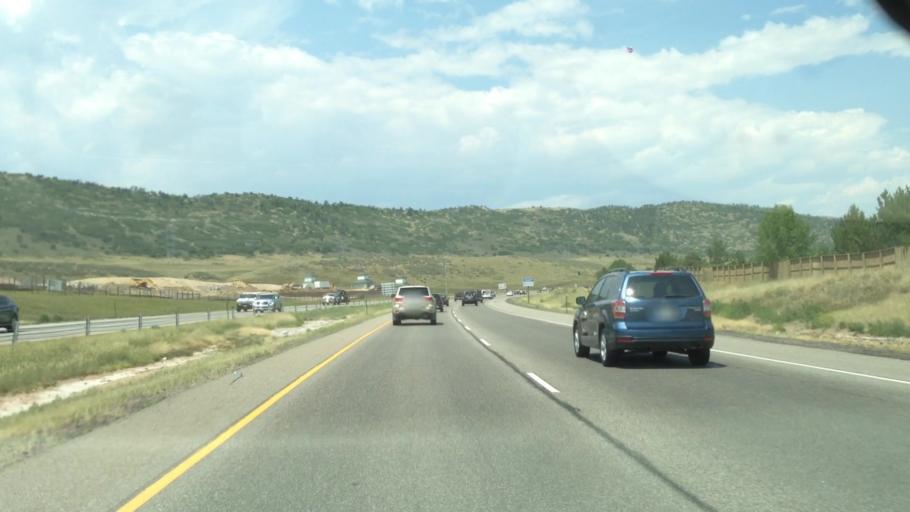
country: US
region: Colorado
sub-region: Jefferson County
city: Ken Caryl
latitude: 39.5608
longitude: -105.1187
